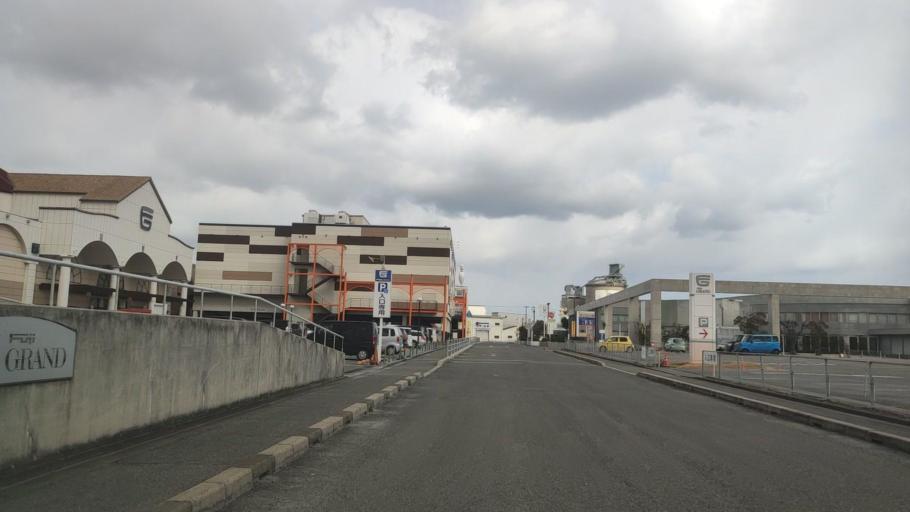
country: JP
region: Ehime
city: Saijo
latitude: 34.0605
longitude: 133.0149
